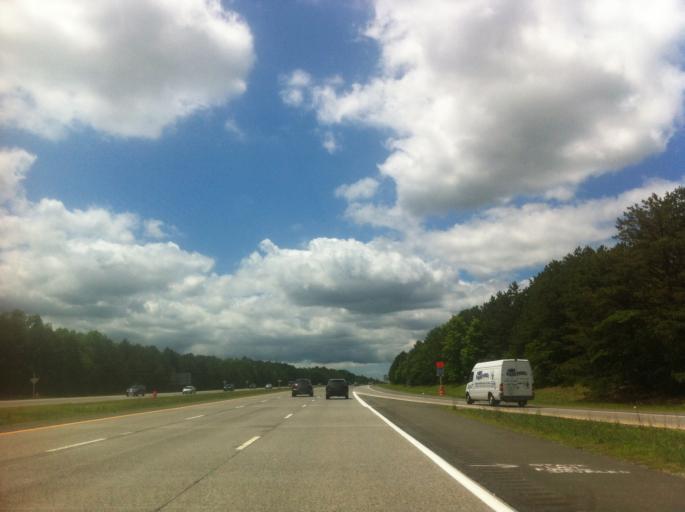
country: US
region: New York
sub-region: Suffolk County
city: Calverton
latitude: 40.9004
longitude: -72.7435
